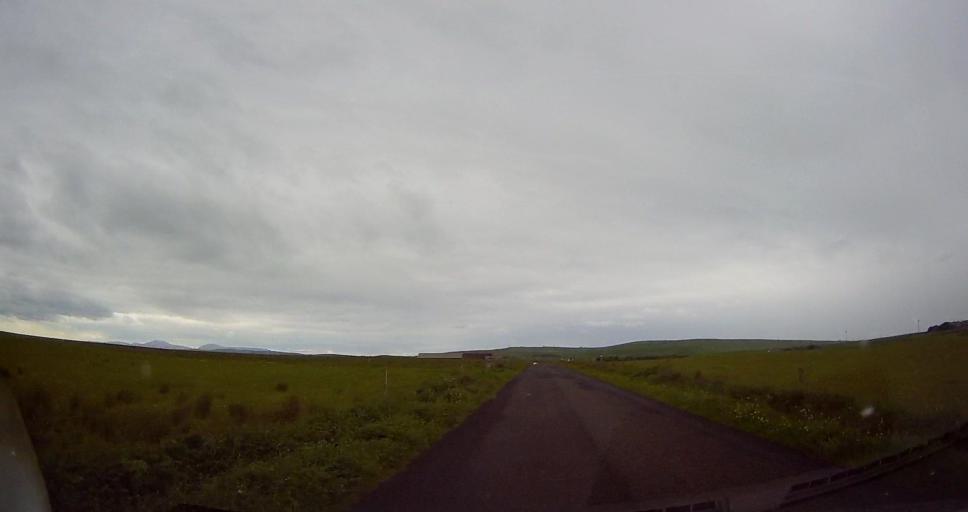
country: GB
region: Scotland
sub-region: Orkney Islands
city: Stromness
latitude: 59.0999
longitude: -3.2650
